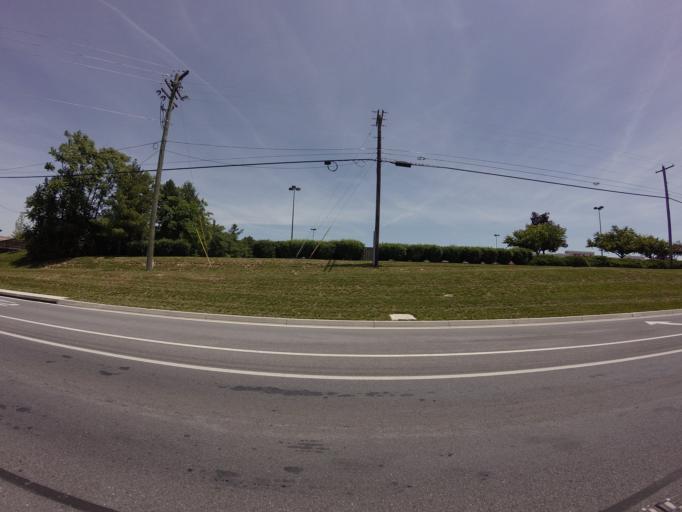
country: US
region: Maryland
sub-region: Frederick County
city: Frederick
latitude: 39.3854
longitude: -77.4025
